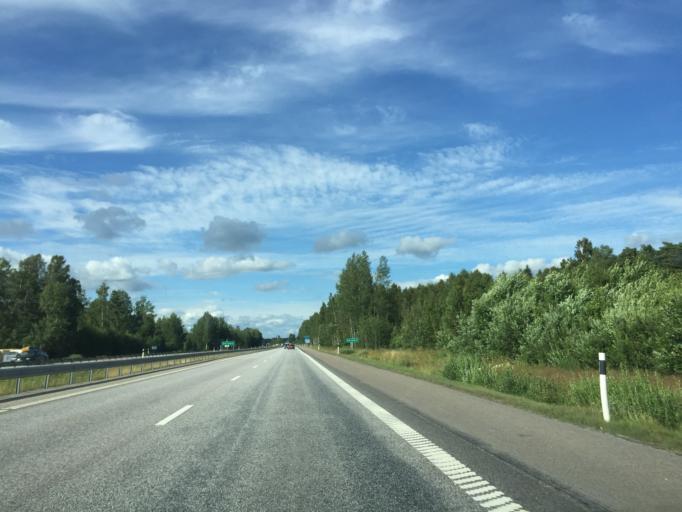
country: SE
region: OErebro
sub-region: Orebro Kommun
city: Orebro
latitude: 59.2229
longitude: 15.1376
